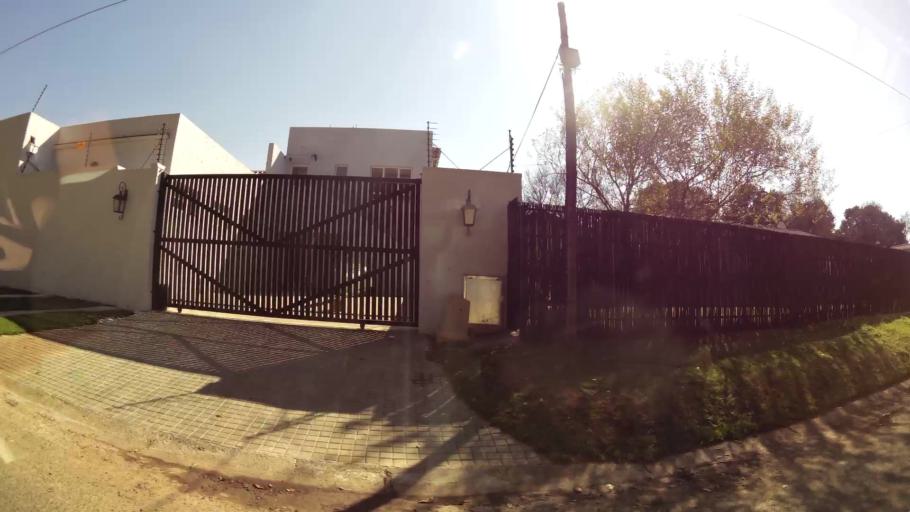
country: ZA
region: Gauteng
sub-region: City of Johannesburg Metropolitan Municipality
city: Johannesburg
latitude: -26.1449
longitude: 28.0996
